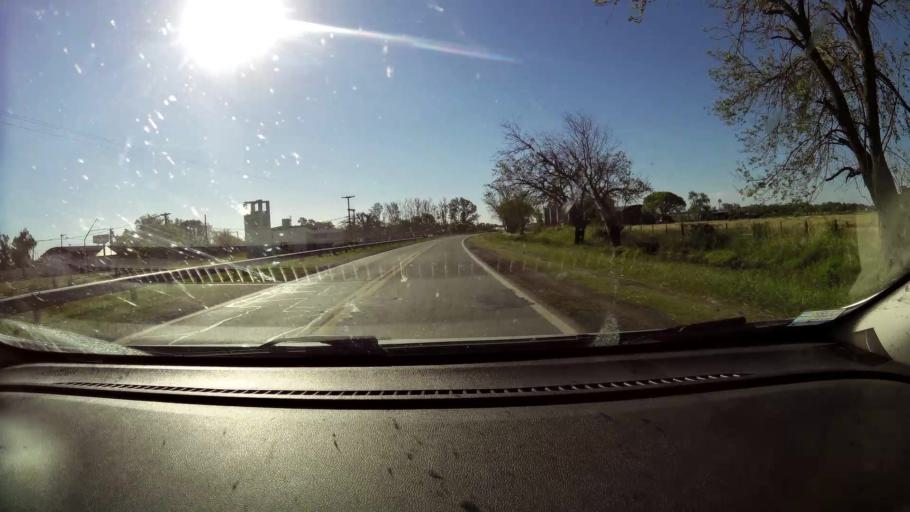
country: AR
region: Cordoba
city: San Francisco
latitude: -31.4237
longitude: -62.0549
